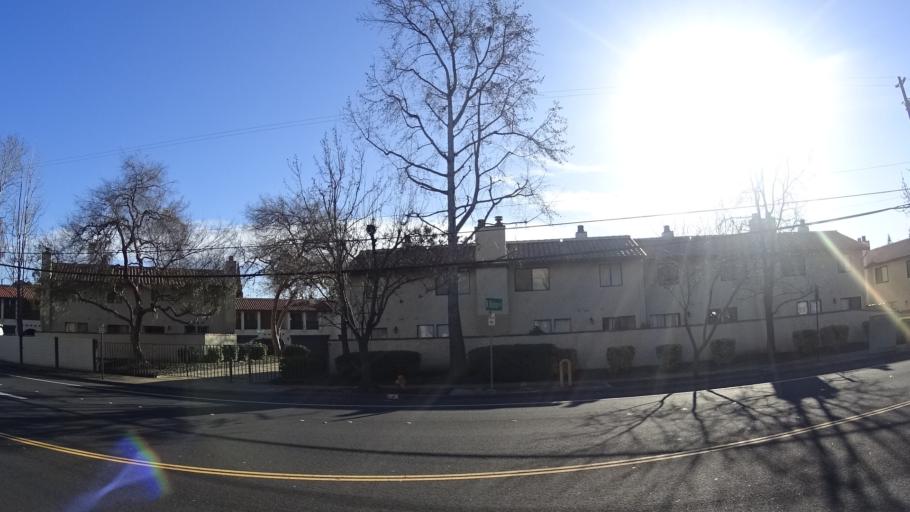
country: US
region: California
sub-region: Alameda County
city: Hayward
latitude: 37.6583
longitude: -122.0990
